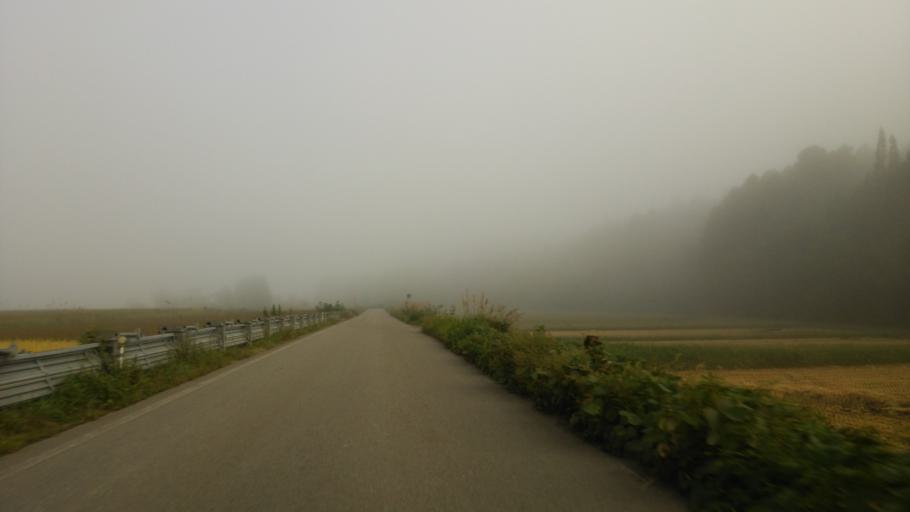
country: JP
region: Fukushima
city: Kitakata
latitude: 37.5826
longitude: 139.7753
